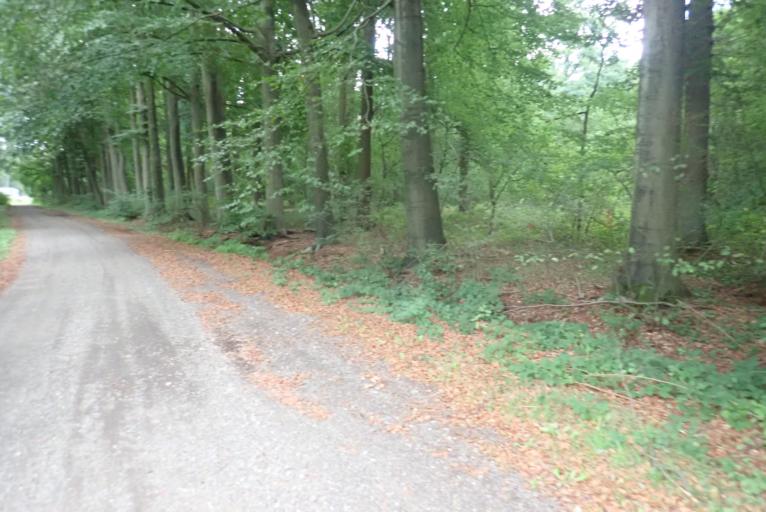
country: BE
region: Flanders
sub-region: Provincie Antwerpen
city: Ranst
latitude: 51.1973
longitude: 4.5899
